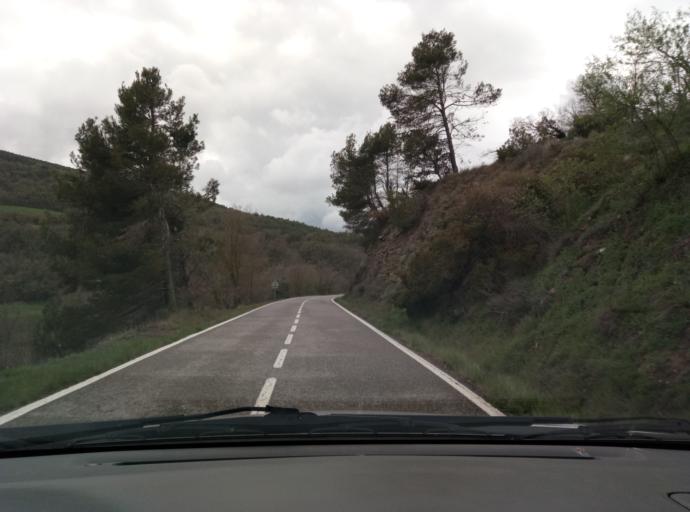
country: ES
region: Catalonia
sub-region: Provincia de Tarragona
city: Conesa
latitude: 41.5583
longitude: 1.3058
